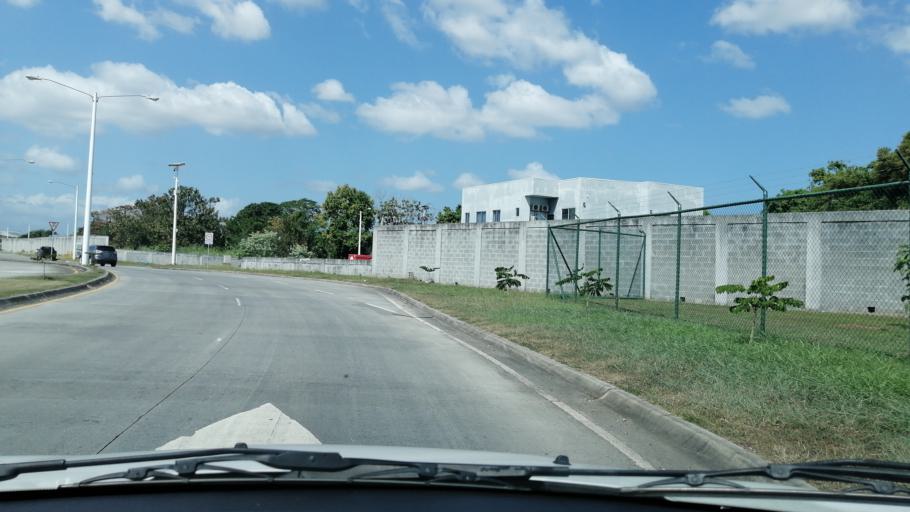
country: PA
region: Panama
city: San Miguelito
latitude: 9.0384
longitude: -79.4336
